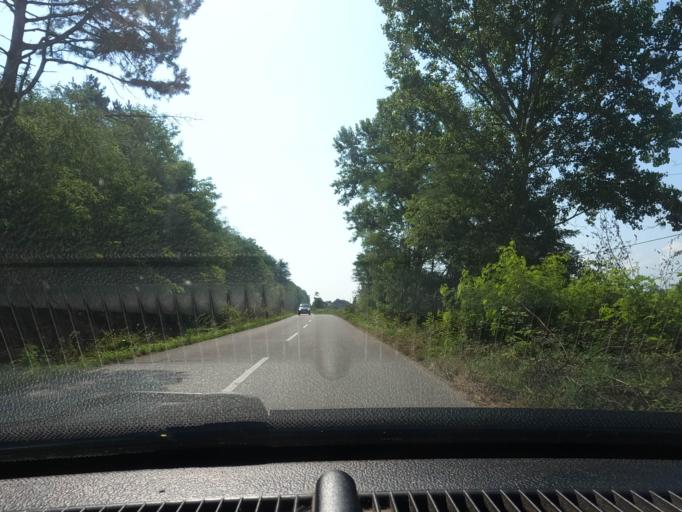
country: RS
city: Kozjak
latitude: 44.5566
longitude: 19.3185
